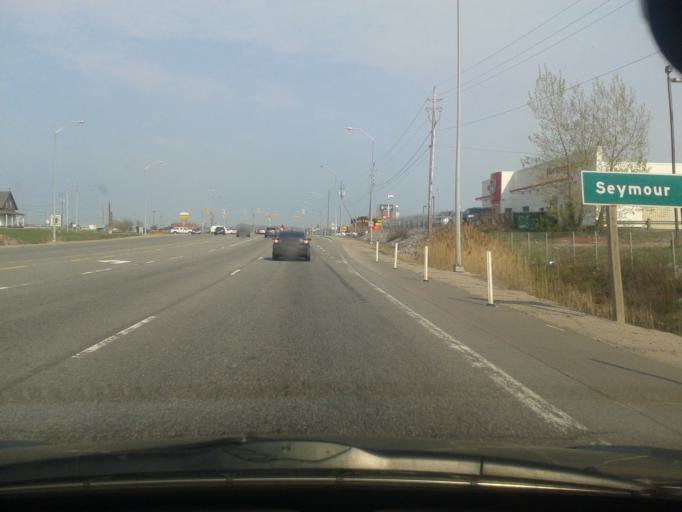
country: CA
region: Ontario
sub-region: Nipissing District
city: North Bay
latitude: 46.3083
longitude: -79.4363
